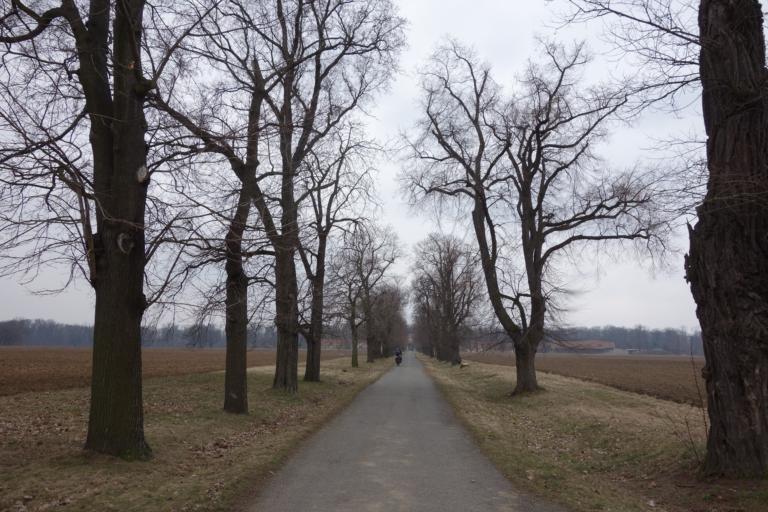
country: CZ
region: Central Bohemia
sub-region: Okres Melnik
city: Veltrusy
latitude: 50.2823
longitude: 14.3312
